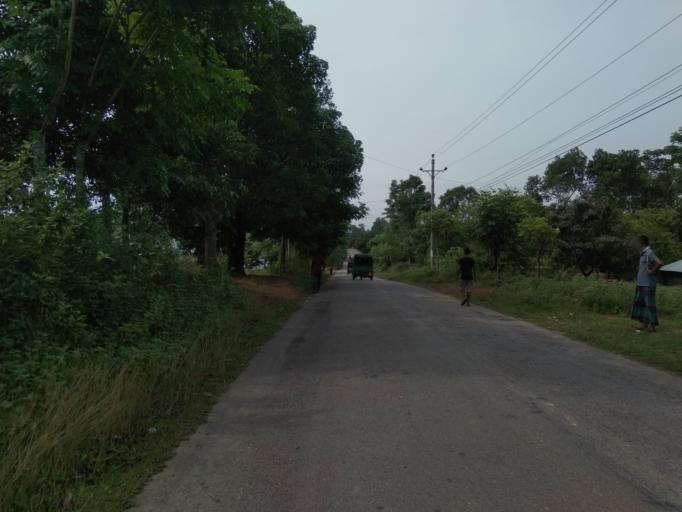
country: BD
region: Chittagong
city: Khagrachhari
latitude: 22.9990
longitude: 92.0111
